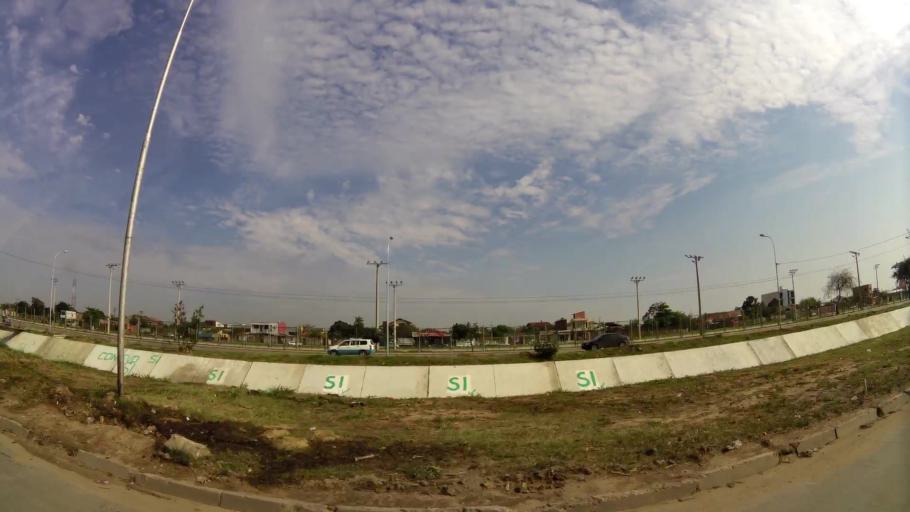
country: BO
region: Santa Cruz
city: Santa Cruz de la Sierra
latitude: -17.7323
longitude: -63.1383
